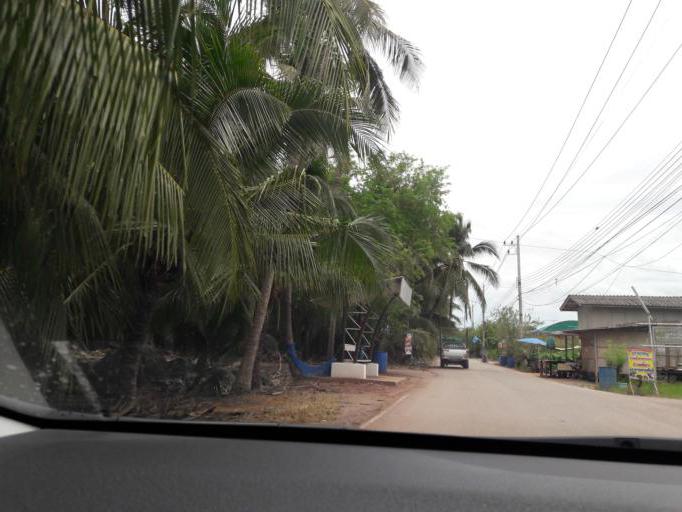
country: TH
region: Samut Sakhon
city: Ban Phaeo
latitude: 13.5463
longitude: 100.0411
